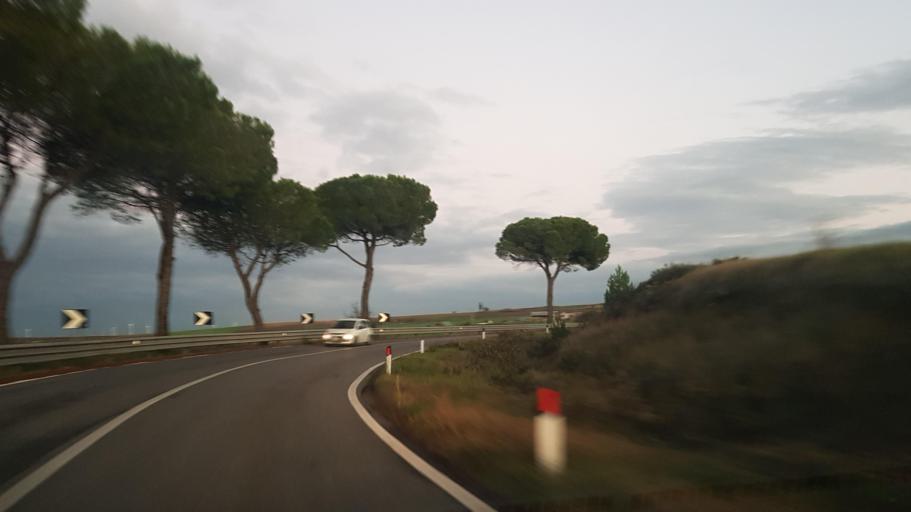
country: IT
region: Basilicate
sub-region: Provincia di Matera
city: Matera
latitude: 40.6773
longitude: 16.6766
